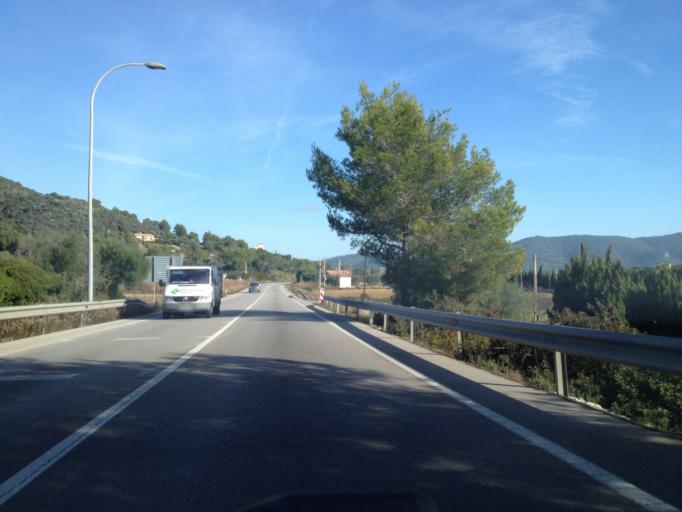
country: ES
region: Balearic Islands
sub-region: Illes Balears
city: Son Servera
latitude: 39.6347
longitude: 3.3659
